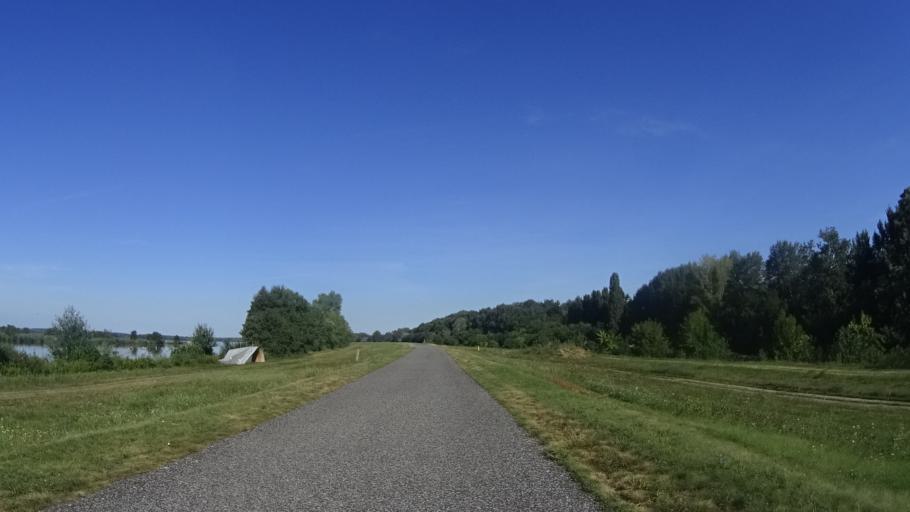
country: SK
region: Bratislavsky
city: Dunajska Luzna
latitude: 48.0561
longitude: 17.2289
